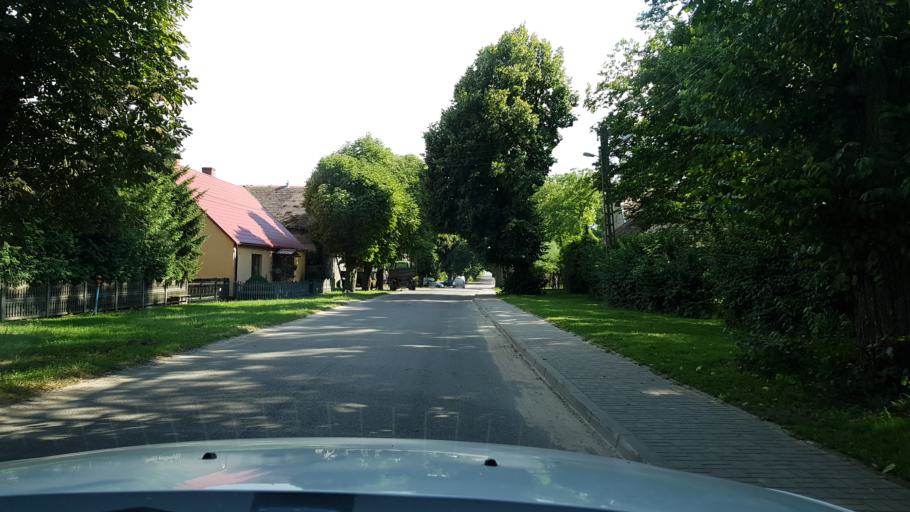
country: PL
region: West Pomeranian Voivodeship
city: Trzcinsko Zdroj
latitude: 52.9544
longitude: 14.5491
